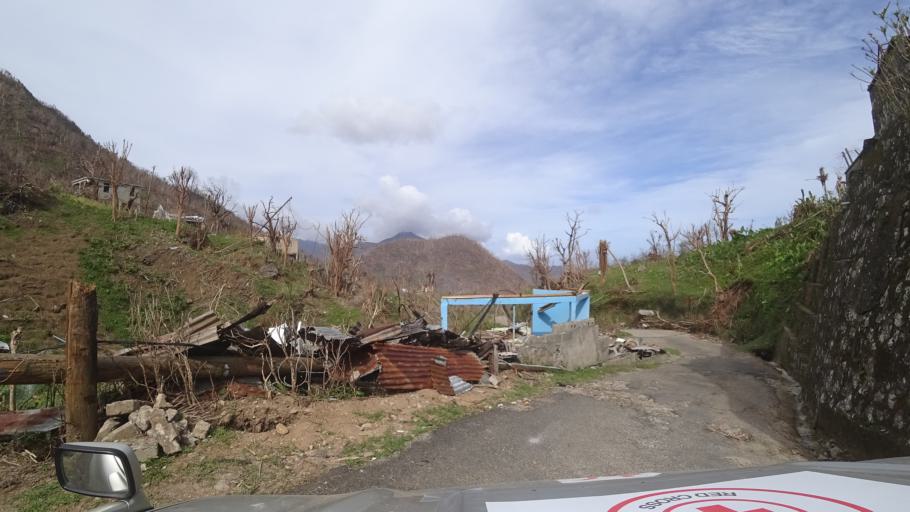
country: DM
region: Saint Mark
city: Soufriere
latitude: 15.2363
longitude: -61.3386
